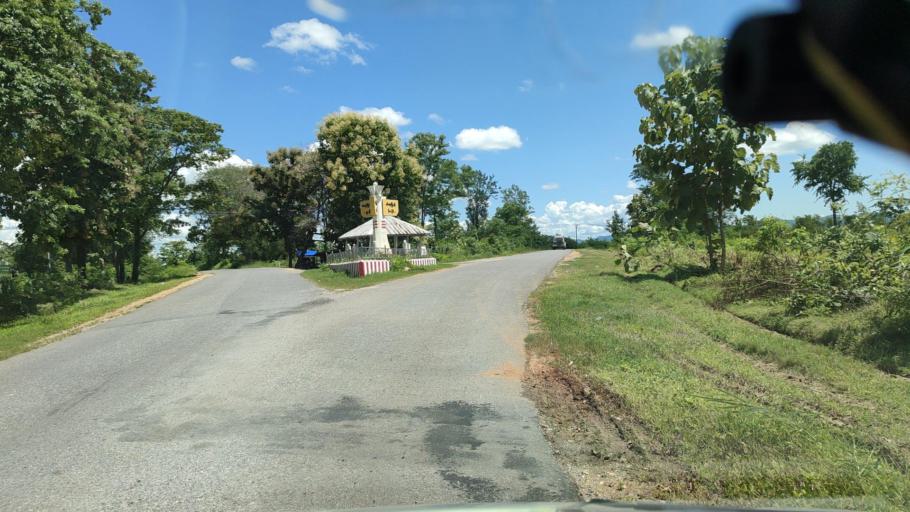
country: MM
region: Magway
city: Thayetmyo
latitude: 19.3684
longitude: 95.1021
